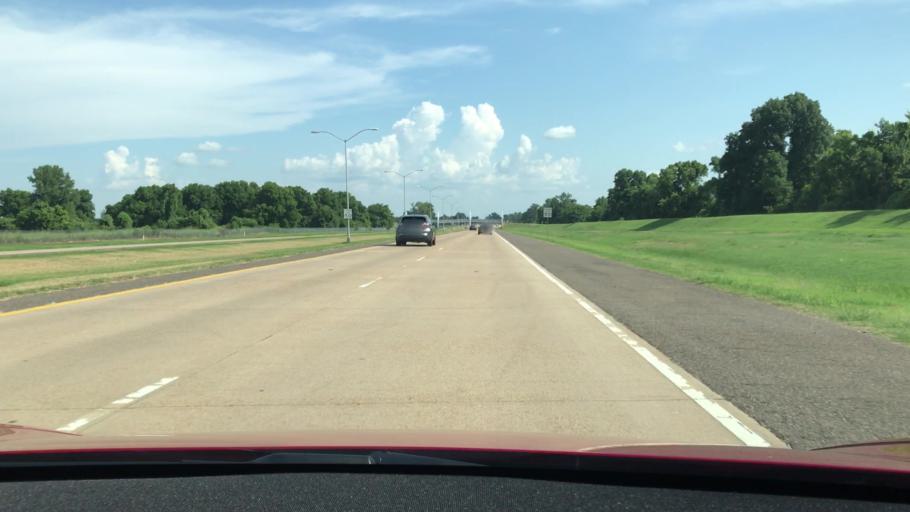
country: US
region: Louisiana
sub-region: Bossier Parish
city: Bossier City
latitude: 32.4749
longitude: -93.6789
